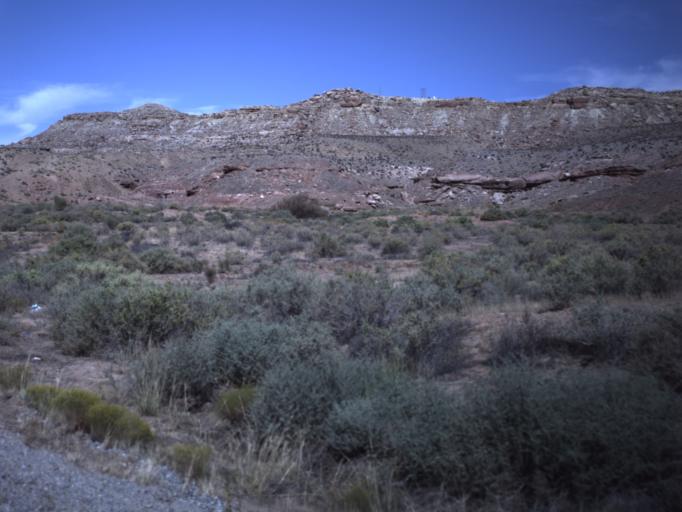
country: US
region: Utah
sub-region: San Juan County
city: Blanding
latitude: 37.2348
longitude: -109.2225
